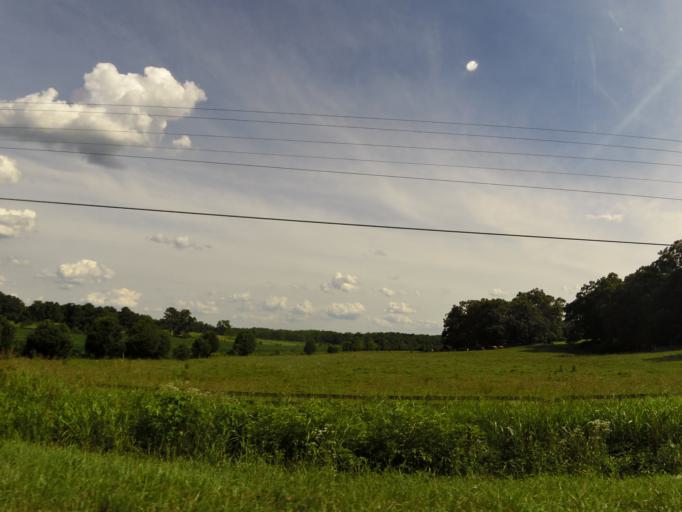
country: US
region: Tennessee
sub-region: Carroll County
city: Huntingdon
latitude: 36.0311
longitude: -88.3451
